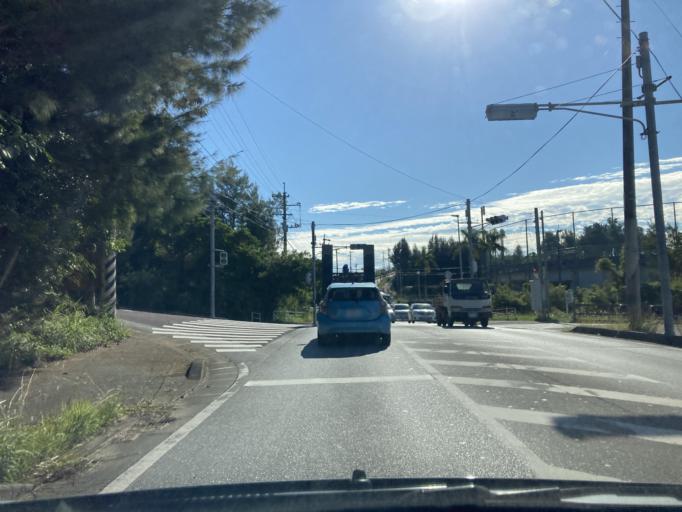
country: JP
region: Okinawa
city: Okinawa
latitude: 26.3708
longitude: 127.7696
